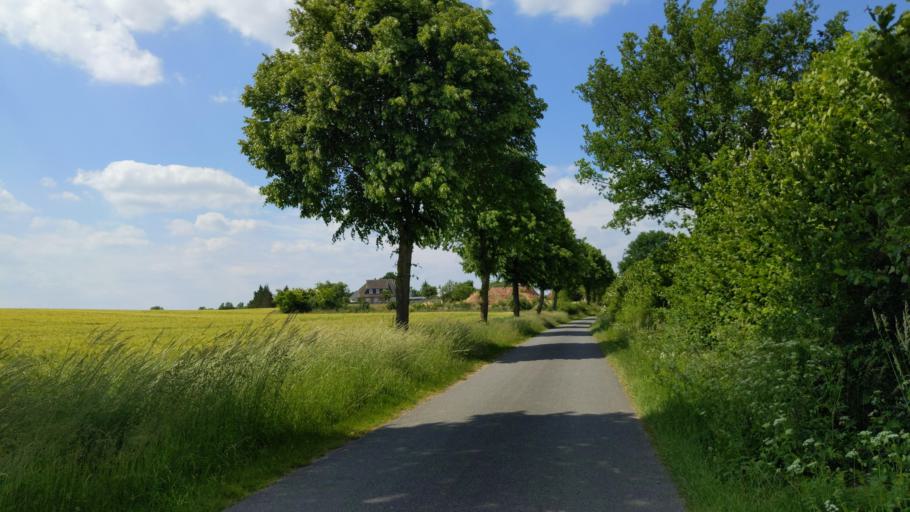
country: DE
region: Schleswig-Holstein
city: Kulpin
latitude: 53.7055
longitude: 10.7024
